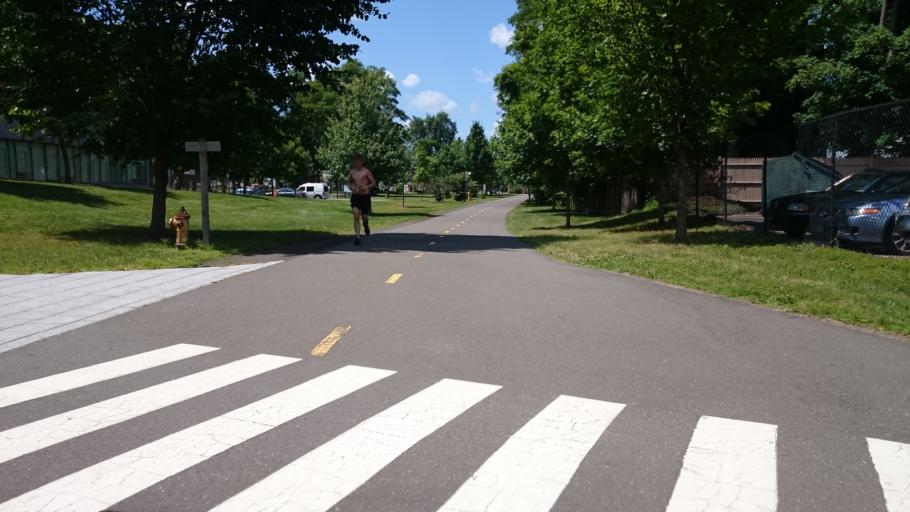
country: US
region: Connecticut
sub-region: New Haven County
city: New Haven
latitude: 41.3161
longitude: -72.9271
